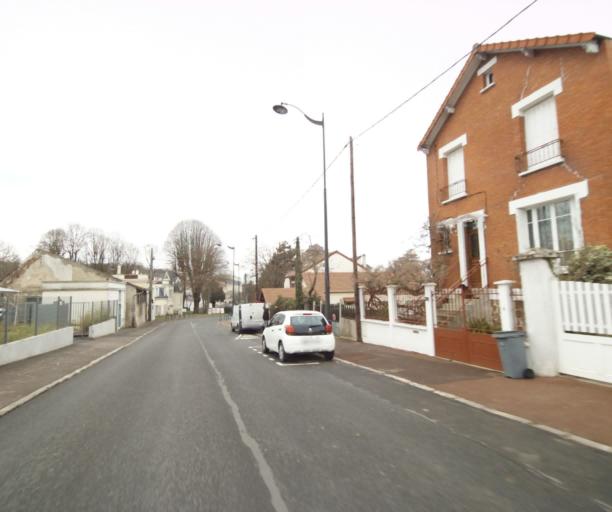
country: FR
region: Ile-de-France
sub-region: Departement des Hauts-de-Seine
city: Garches
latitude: 48.8581
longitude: 2.1842
